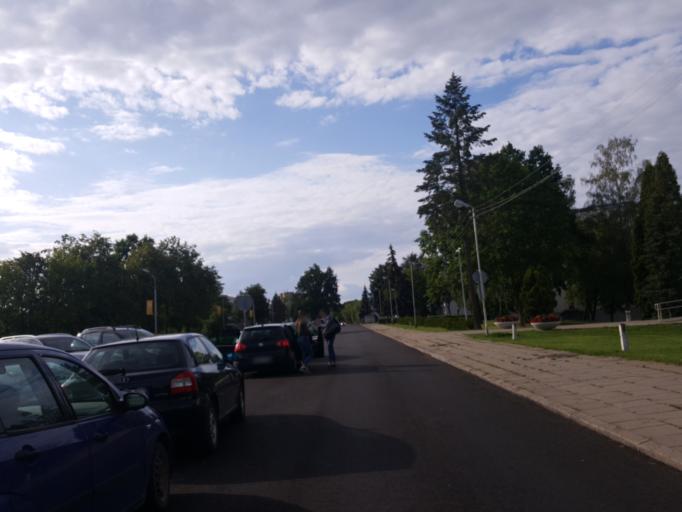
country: LT
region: Kauno apskritis
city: Dainava (Kaunas)
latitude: 54.9017
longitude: 23.9612
